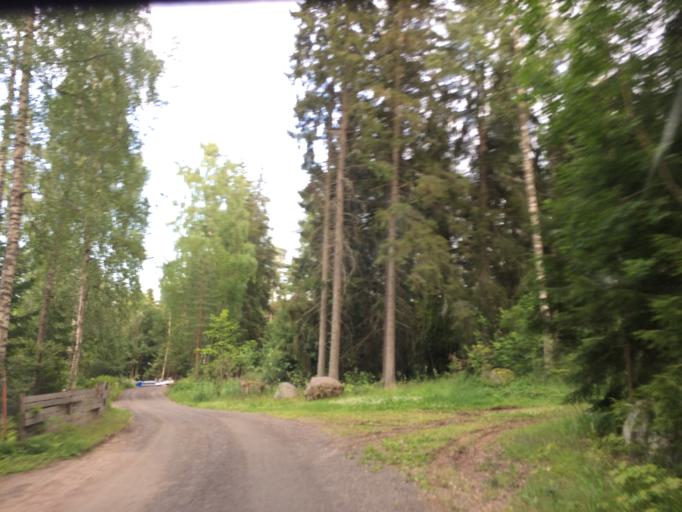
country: FI
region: Haeme
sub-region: Haemeenlinna
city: Tervakoski
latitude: 60.8561
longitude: 24.6220
